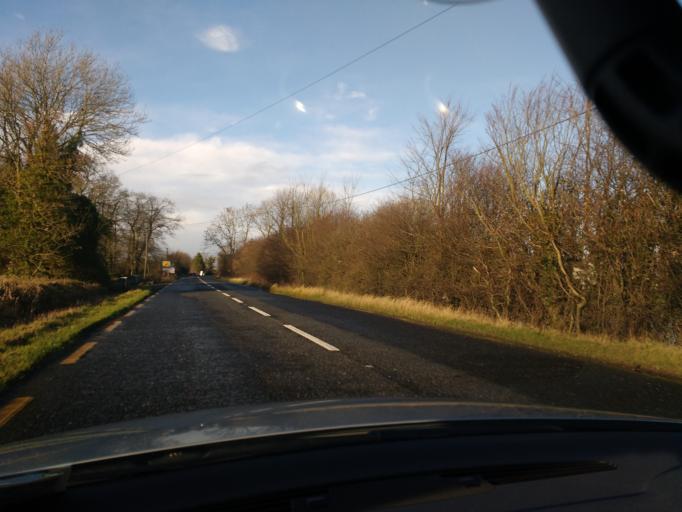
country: IE
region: Munster
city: Thurles
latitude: 52.6483
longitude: -7.7952
